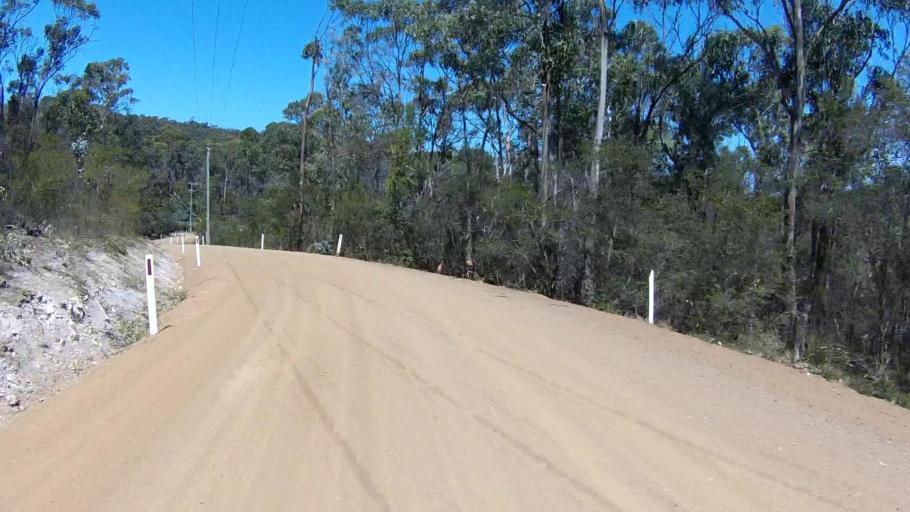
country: AU
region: Tasmania
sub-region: Clarence
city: Lauderdale
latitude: -42.9408
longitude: 147.4604
